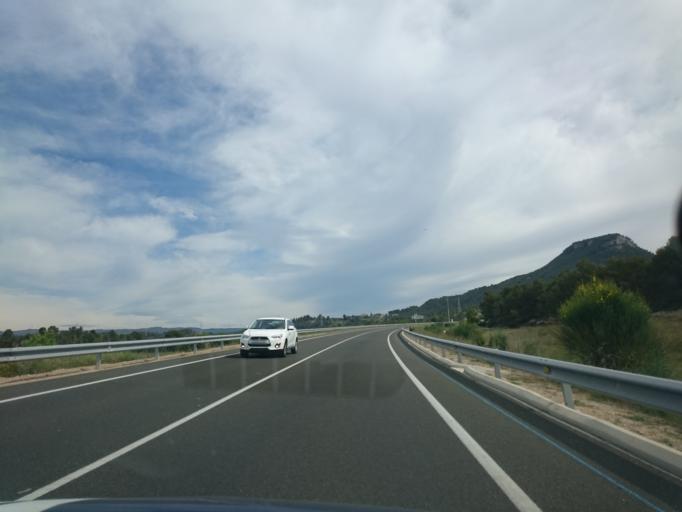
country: ES
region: Catalonia
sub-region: Provincia de Barcelona
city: Odena
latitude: 41.5935
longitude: 1.6620
